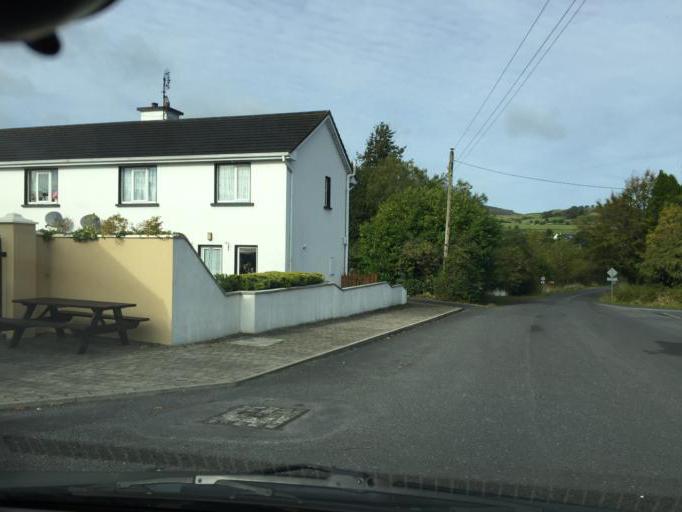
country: IE
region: Connaught
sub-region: Roscommon
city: Boyle
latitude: 54.0275
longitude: -8.3344
